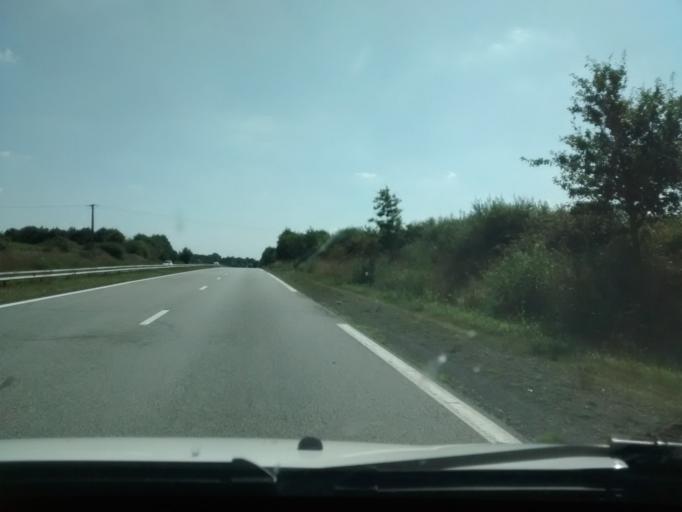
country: FR
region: Brittany
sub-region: Departement d'Ille-et-Vilaine
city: Quedillac
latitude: 48.2408
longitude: -2.1284
